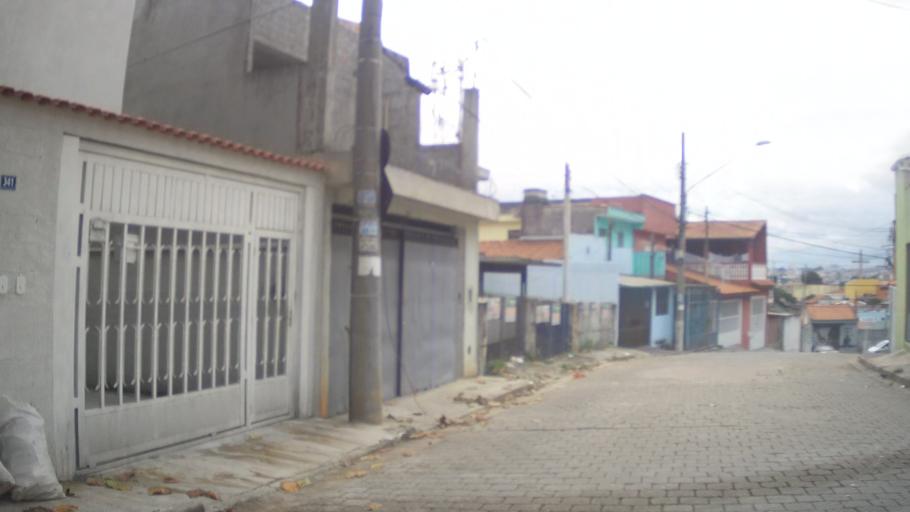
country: BR
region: Sao Paulo
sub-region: Guarulhos
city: Guarulhos
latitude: -23.5008
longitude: -46.5544
